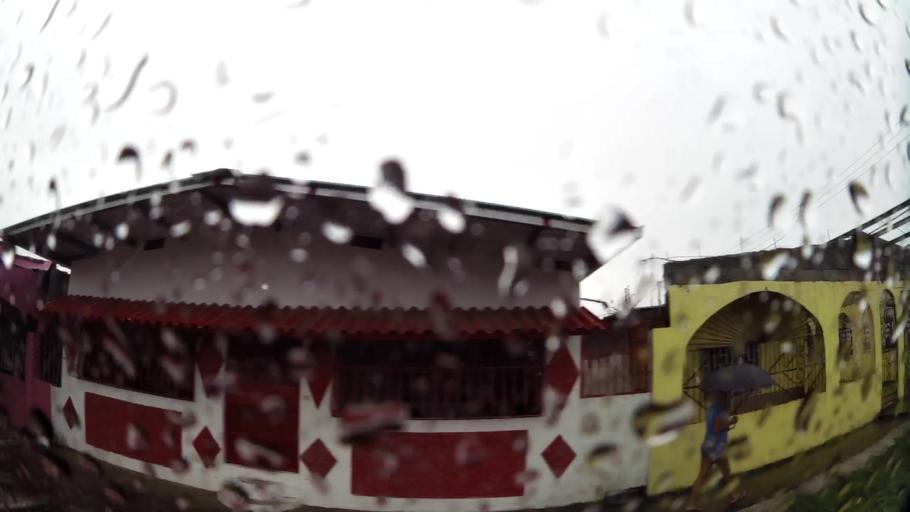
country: PA
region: Colon
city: Sabanitas
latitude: 9.3546
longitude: -79.8064
